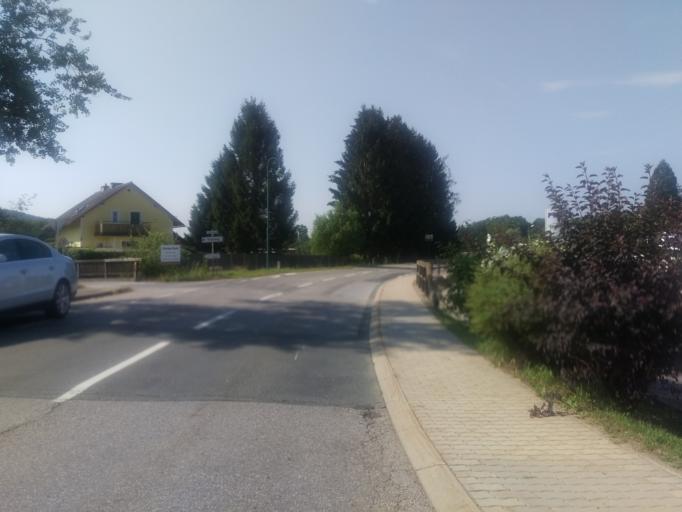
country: AT
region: Styria
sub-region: Politischer Bezirk Graz-Umgebung
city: Fernitz
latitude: 46.9642
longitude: 15.5050
